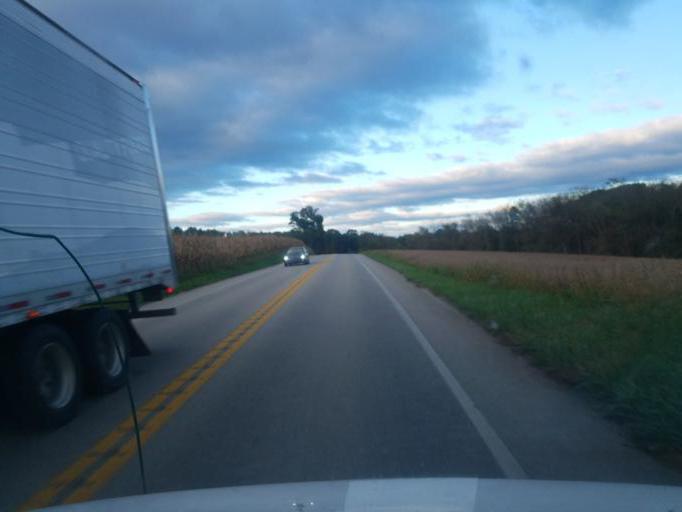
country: US
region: Pennsylvania
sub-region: York County
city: Weigelstown
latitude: 39.9408
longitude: -76.8684
